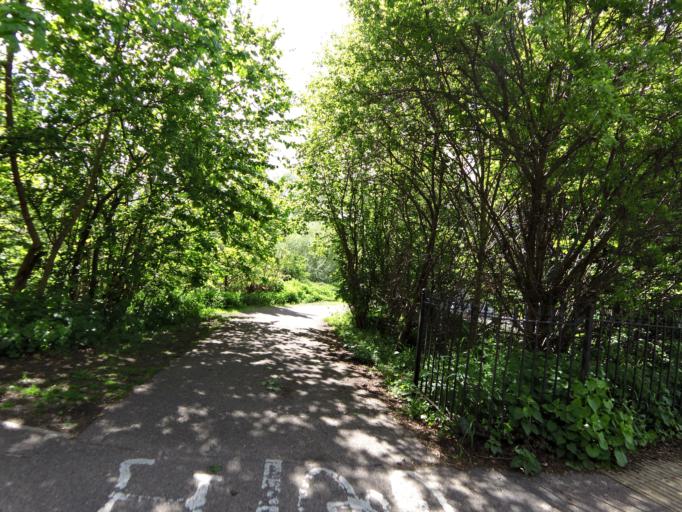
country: GB
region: England
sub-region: Suffolk
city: Bury St Edmunds
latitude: 52.2391
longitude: 0.7122
